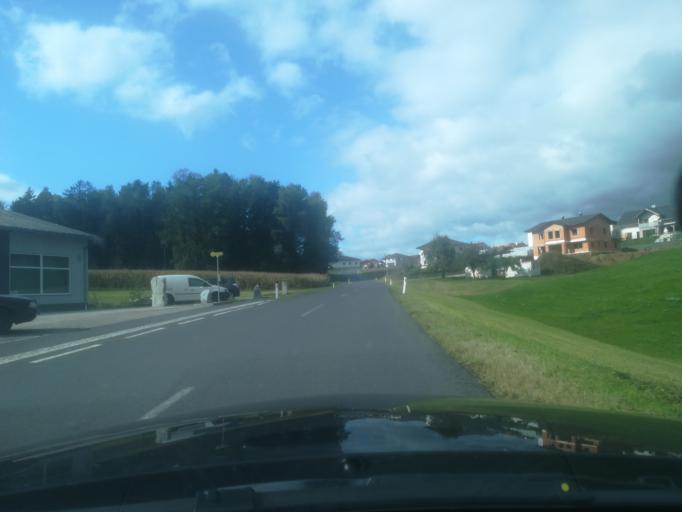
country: AT
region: Upper Austria
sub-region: Politischer Bezirk Urfahr-Umgebung
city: Herzogsdorf
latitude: 48.4306
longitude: 14.1214
